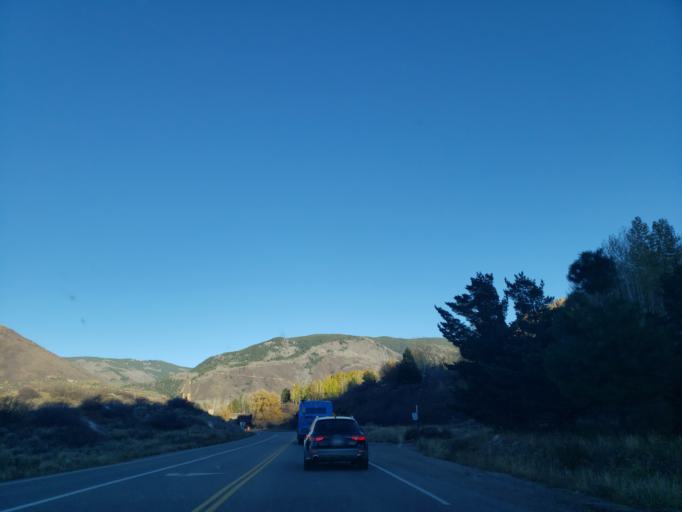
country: US
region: Colorado
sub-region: Pitkin County
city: Aspen
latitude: 39.1932
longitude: -106.8456
